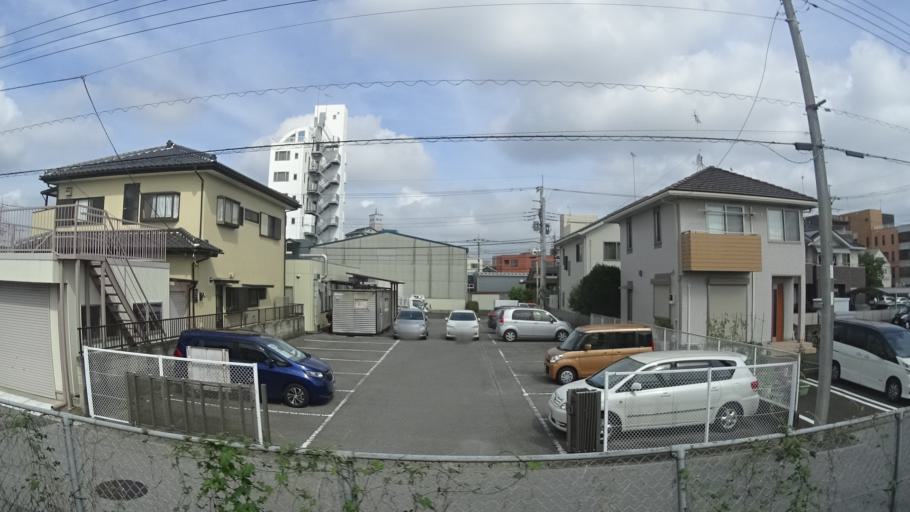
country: JP
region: Tochigi
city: Utsunomiya-shi
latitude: 36.5477
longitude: 139.8907
